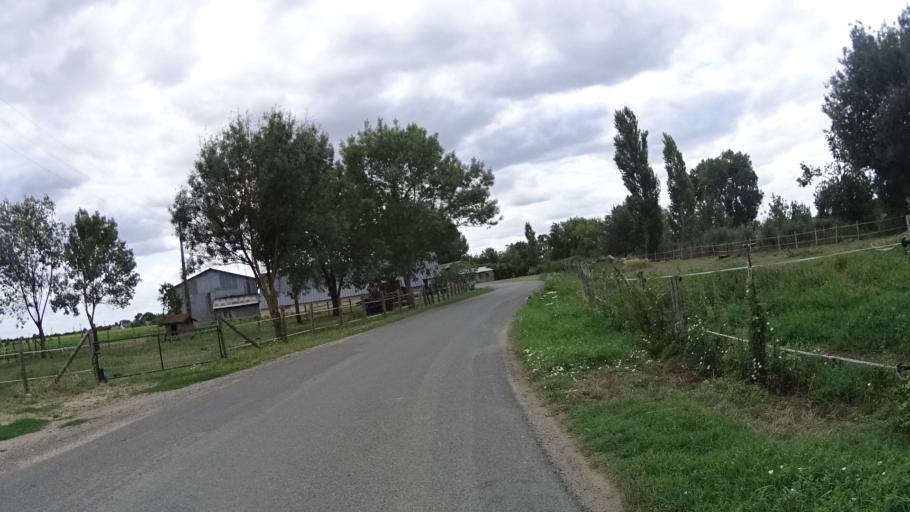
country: FR
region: Pays de la Loire
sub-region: Departement de Maine-et-Loire
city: Les Rosiers-sur-Loire
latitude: 47.3681
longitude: -0.1878
